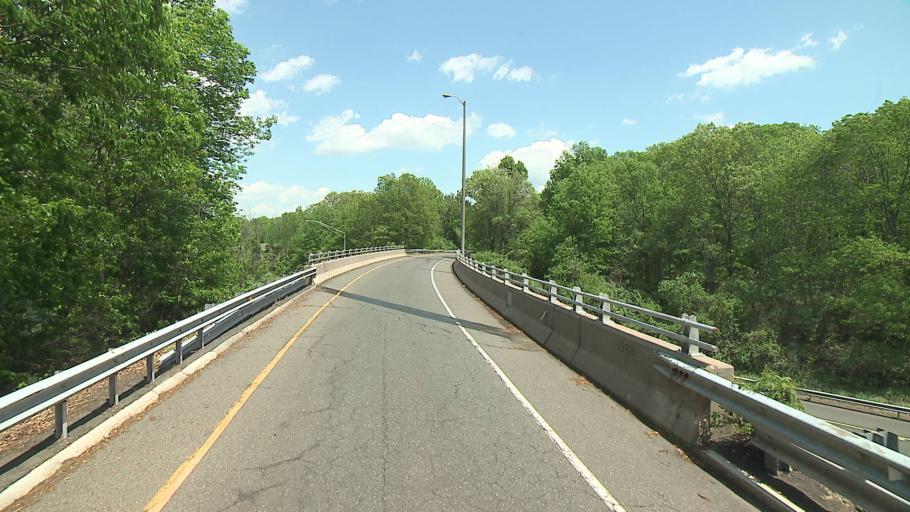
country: US
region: Connecticut
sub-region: Hartford County
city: Plainville
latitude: 41.6755
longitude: -72.8197
